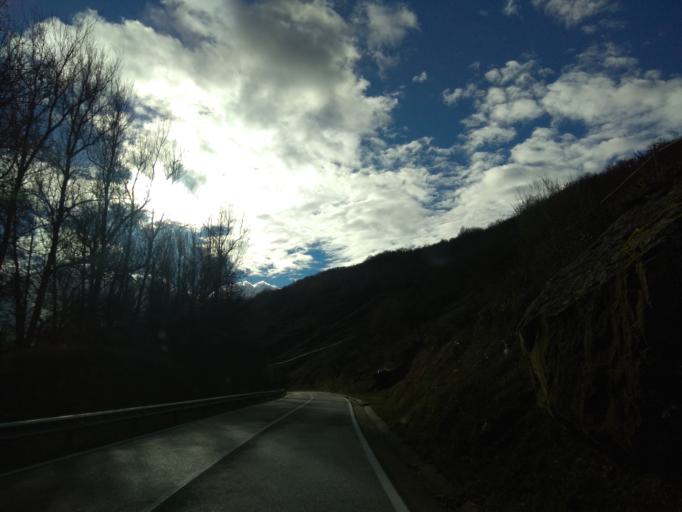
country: ES
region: Cantabria
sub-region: Provincia de Cantabria
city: San Martin de Elines
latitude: 42.8665
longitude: -3.9127
